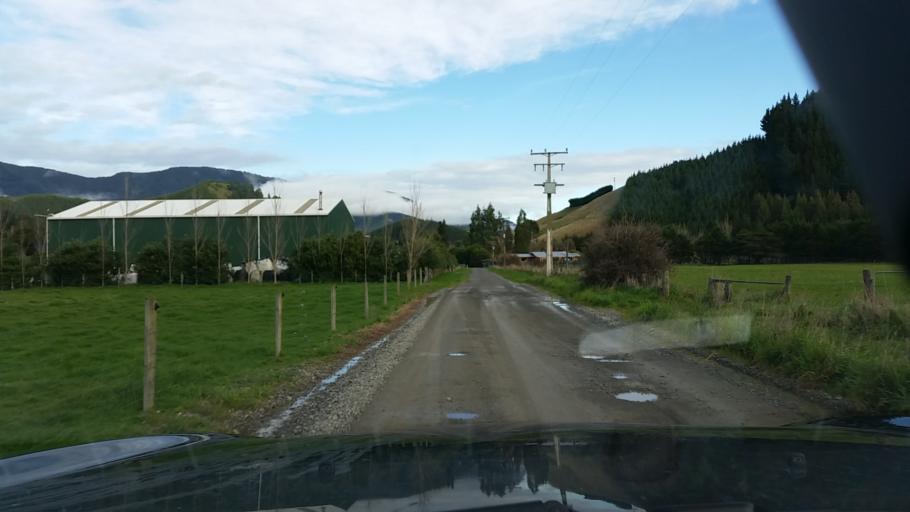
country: NZ
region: Marlborough
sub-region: Marlborough District
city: Picton
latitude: -41.3178
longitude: 173.9683
